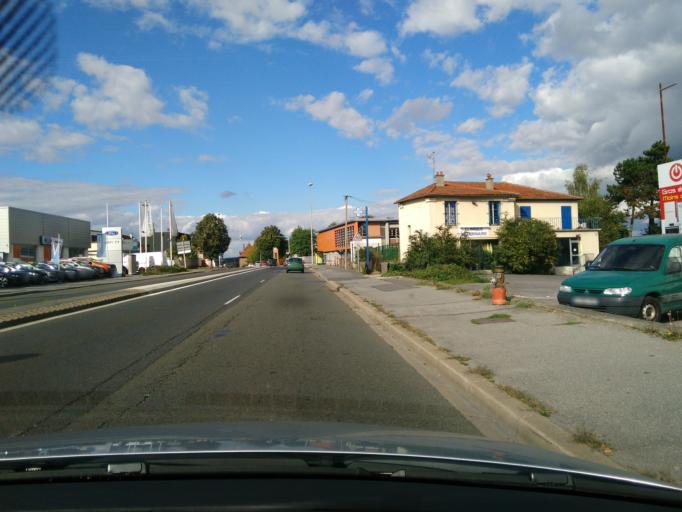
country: FR
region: Ile-de-France
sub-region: Departement de Seine-et-Marne
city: Meaux
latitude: 48.9475
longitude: 2.8799
